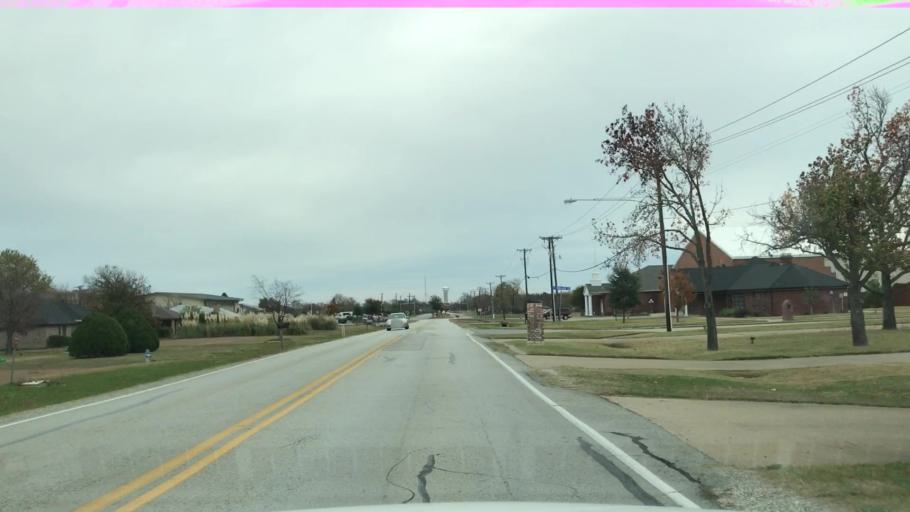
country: US
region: Texas
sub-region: Dallas County
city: Sachse
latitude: 32.9732
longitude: -96.5875
